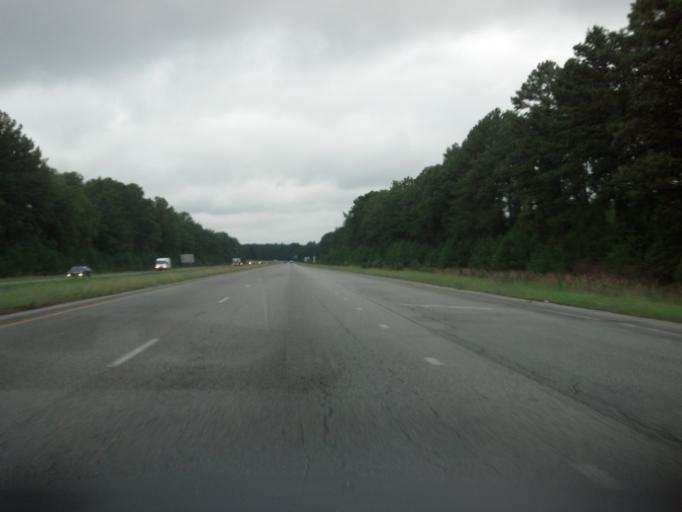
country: US
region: North Carolina
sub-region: Nash County
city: Rocky Mount
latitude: 35.9498
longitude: -77.7617
